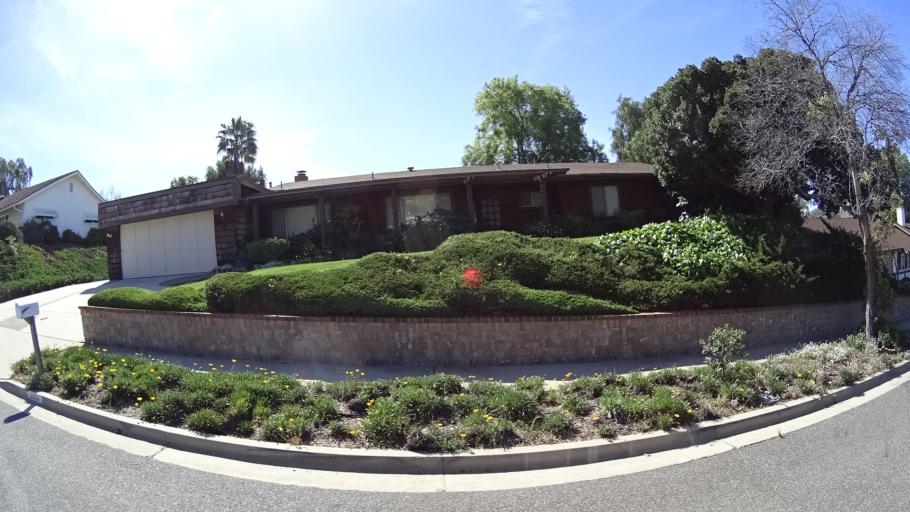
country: US
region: California
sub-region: Ventura County
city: Thousand Oaks
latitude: 34.2206
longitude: -118.8638
